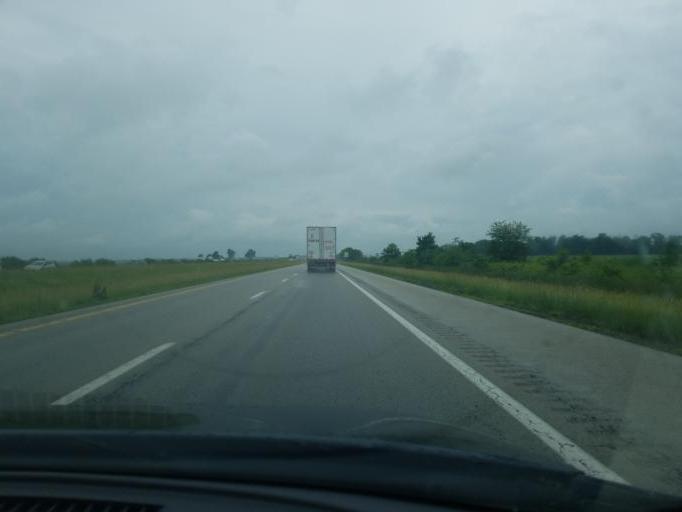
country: US
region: Ohio
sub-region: Greene County
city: Jamestown
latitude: 39.5523
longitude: -83.7327
